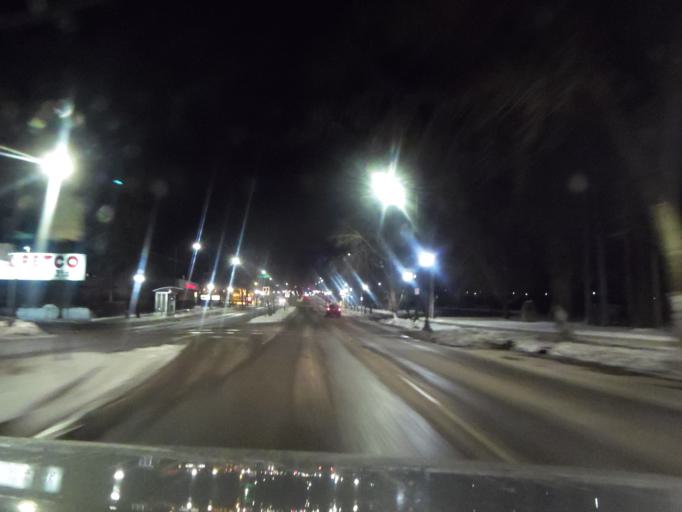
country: US
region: Minnesota
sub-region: Dakota County
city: Mendota Heights
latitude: 44.9179
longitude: -93.1974
